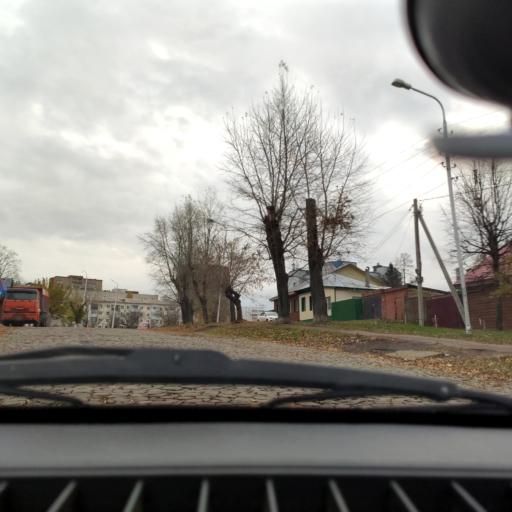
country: RU
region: Bashkortostan
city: Ufa
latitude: 54.7273
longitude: 55.9221
